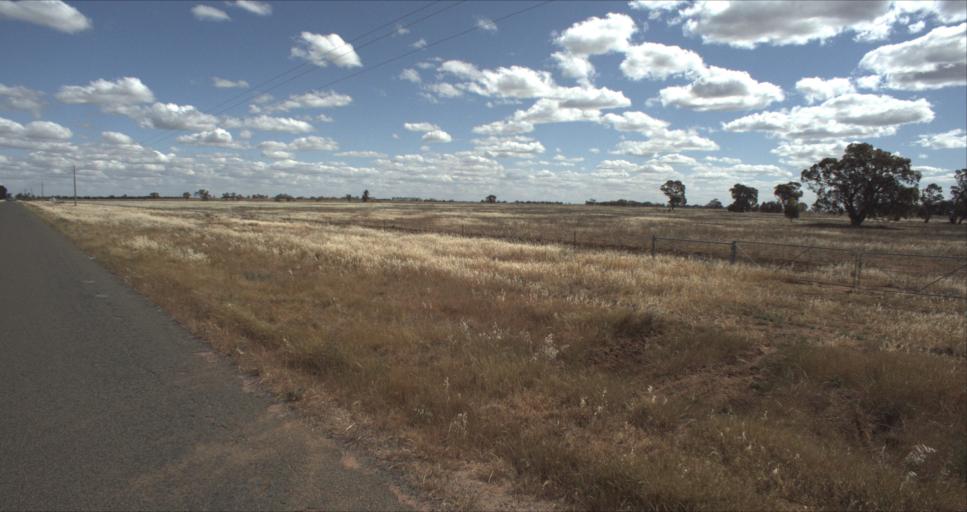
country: AU
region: New South Wales
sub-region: Leeton
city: Leeton
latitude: -34.4654
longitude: 146.2519
